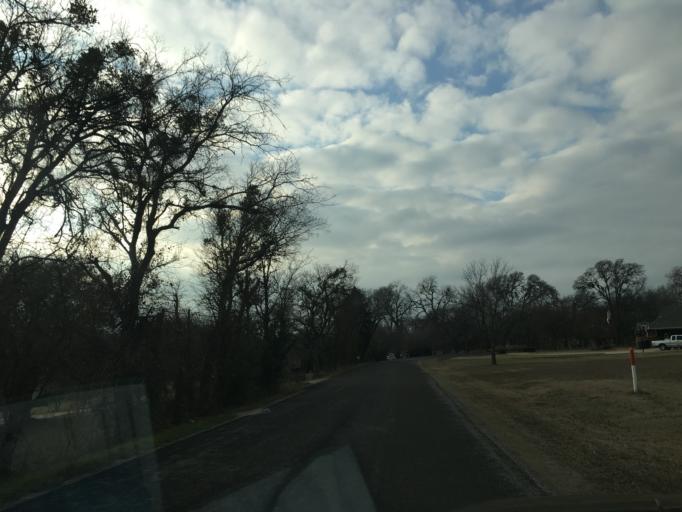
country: US
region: Texas
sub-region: Ellis County
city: Red Oak
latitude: 32.4793
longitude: -96.7875
